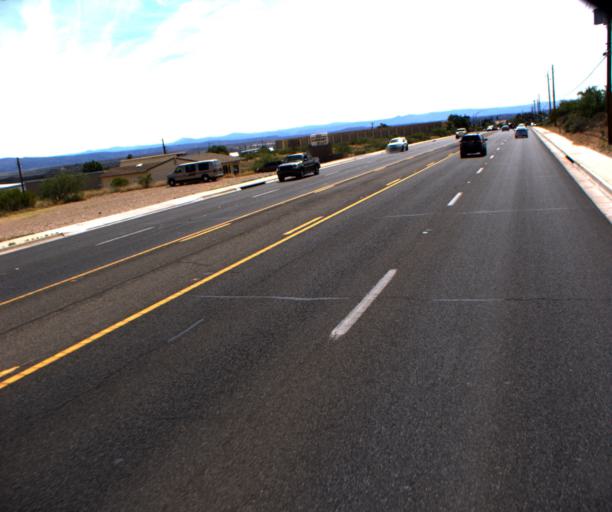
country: US
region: Arizona
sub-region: Yavapai County
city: Cottonwood
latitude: 34.7314
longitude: -112.0262
